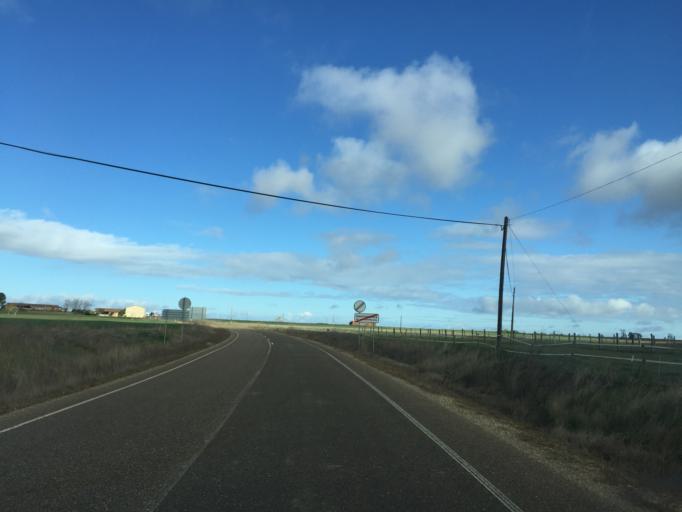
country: ES
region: Castille and Leon
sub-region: Provincia de Zamora
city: Manganeses de la Lampreana
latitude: 41.7535
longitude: -5.7153
